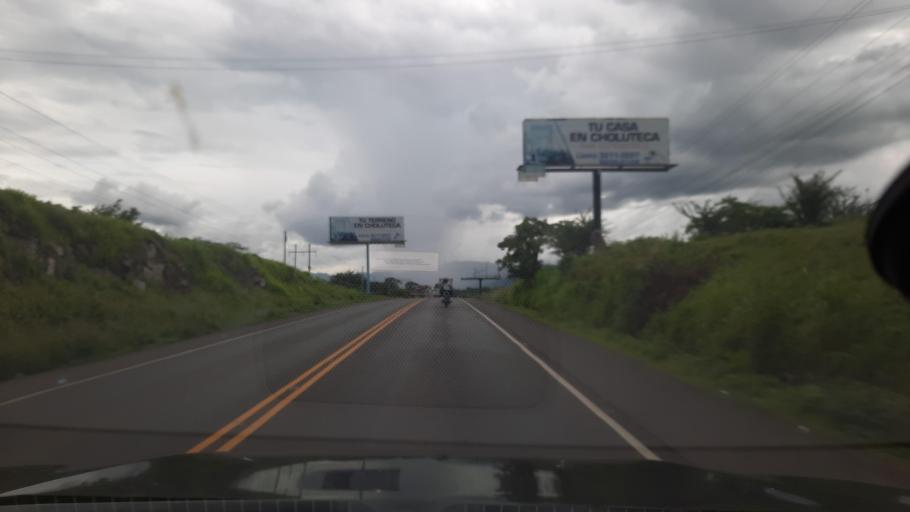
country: HN
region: Choluteca
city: Ciudad Choluteca
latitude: 13.3305
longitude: -87.2285
